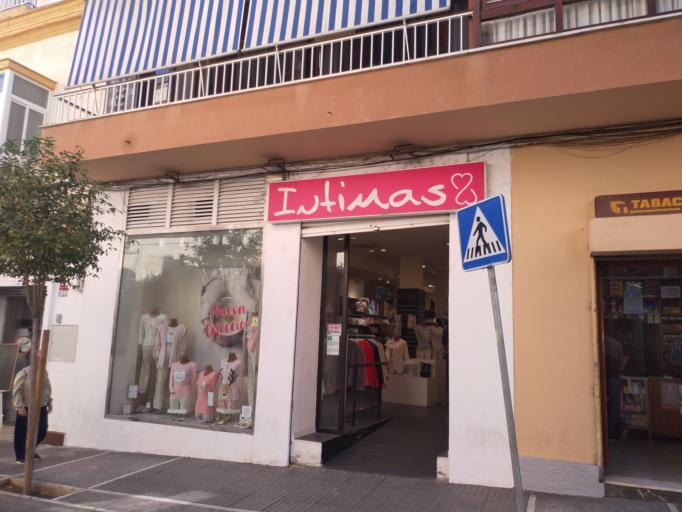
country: ES
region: Andalusia
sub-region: Provincia de Cadiz
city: San Fernando
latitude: 36.4684
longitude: -6.1958
